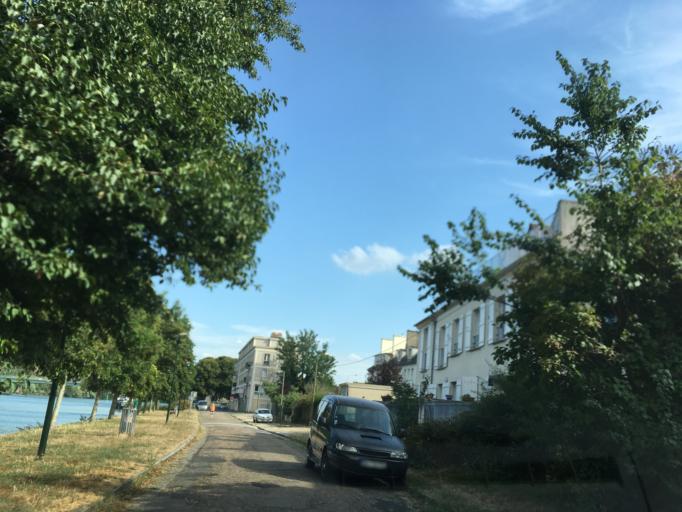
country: FR
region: Haute-Normandie
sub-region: Departement de l'Eure
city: Vernon
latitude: 49.0970
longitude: 1.4816
